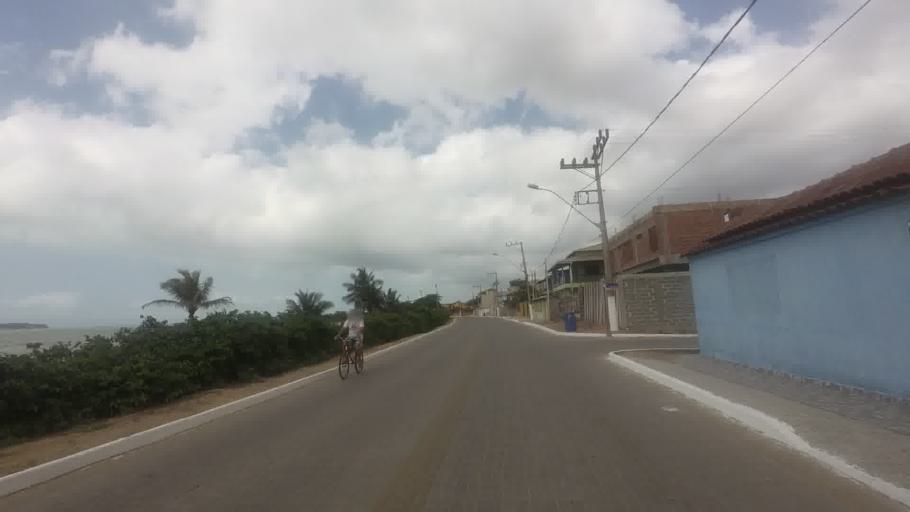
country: BR
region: Espirito Santo
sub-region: Piuma
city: Piuma
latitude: -20.9008
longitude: -40.7774
